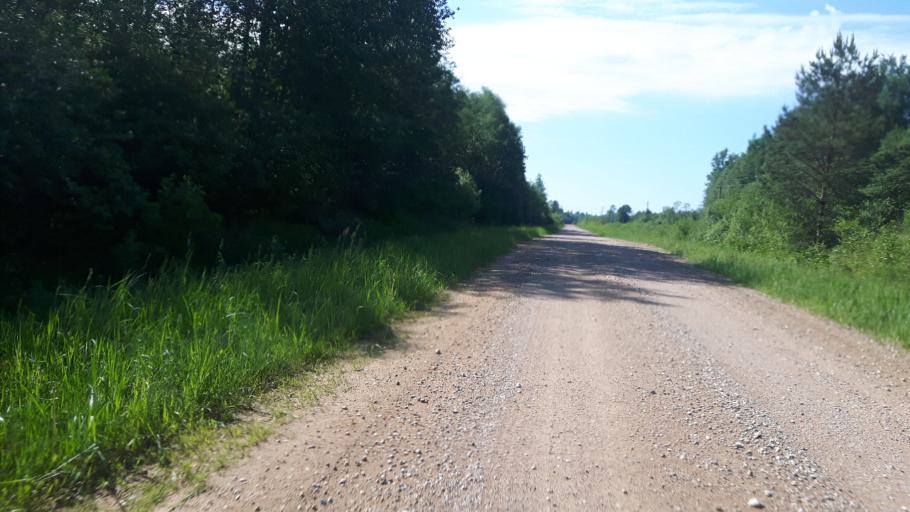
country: EE
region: Paernumaa
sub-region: Vaendra vald (alev)
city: Vandra
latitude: 58.6780
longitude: 25.0318
